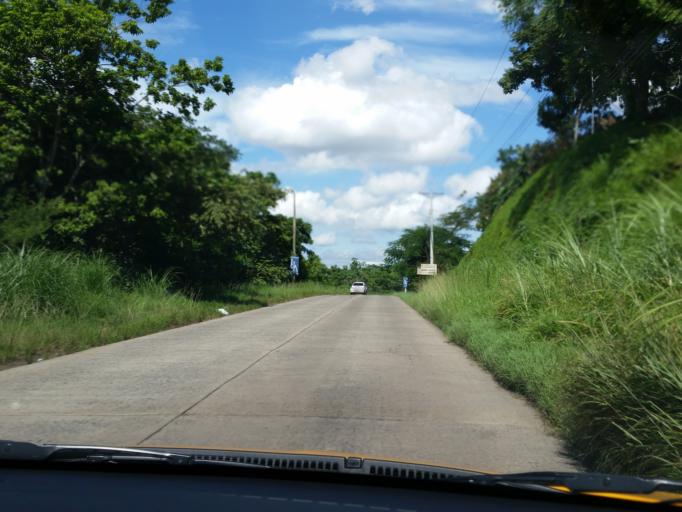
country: PA
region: Panama
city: San Miguelito
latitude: 9.0722
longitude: -79.4690
